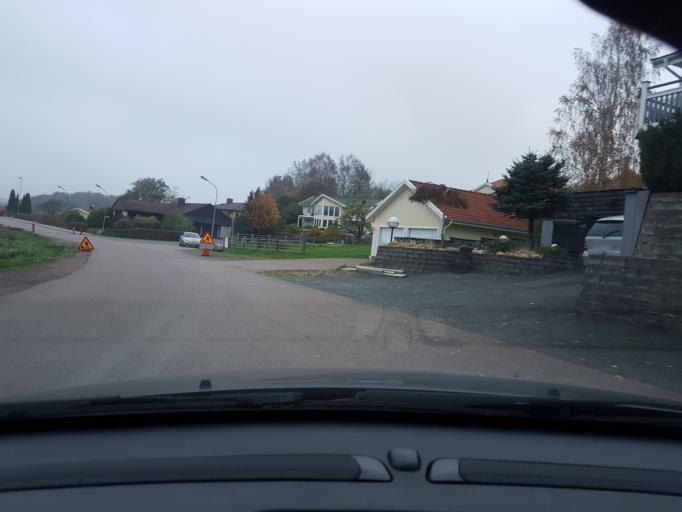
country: SE
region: Vaestra Goetaland
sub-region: Ale Kommun
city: Surte
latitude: 57.8224
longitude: 12.0230
